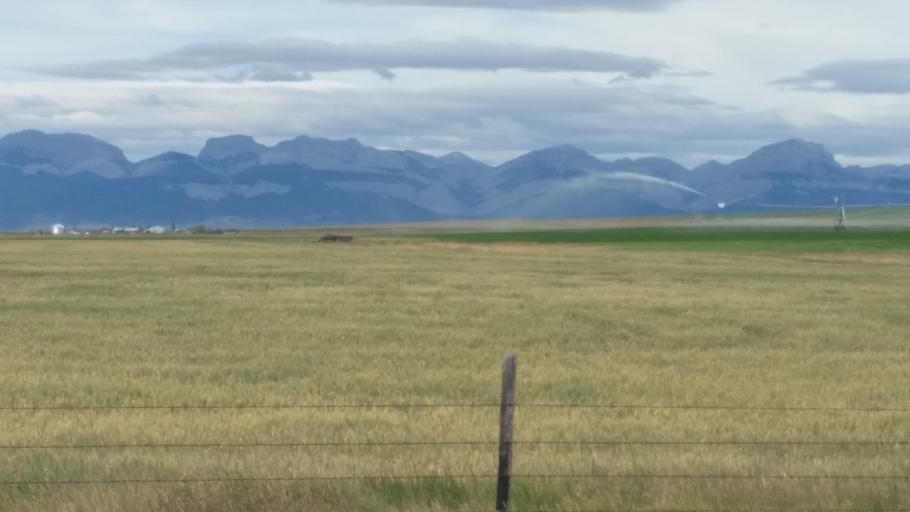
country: US
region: Montana
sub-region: Teton County
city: Choteau
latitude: 48.0164
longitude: -112.3325
